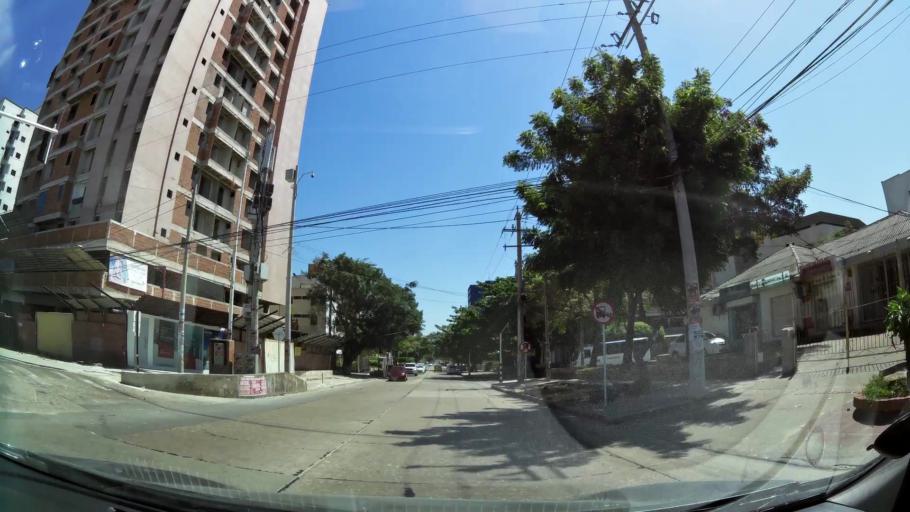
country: CO
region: Atlantico
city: Barranquilla
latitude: 10.9938
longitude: -74.8138
